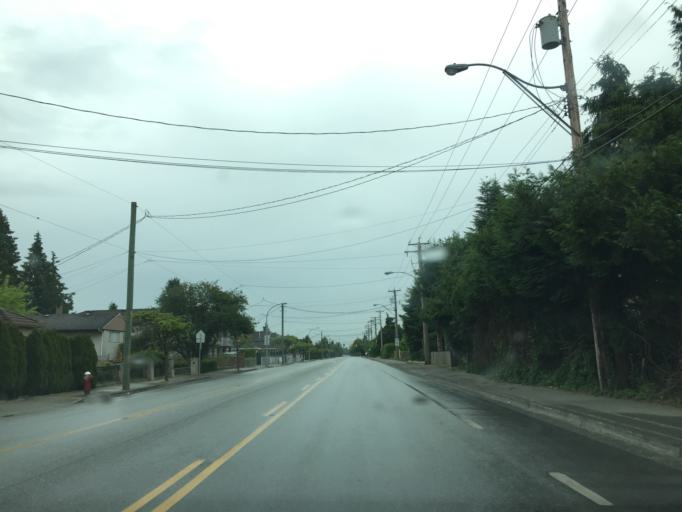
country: CA
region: British Columbia
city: Richmond
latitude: 49.1408
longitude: -123.1189
